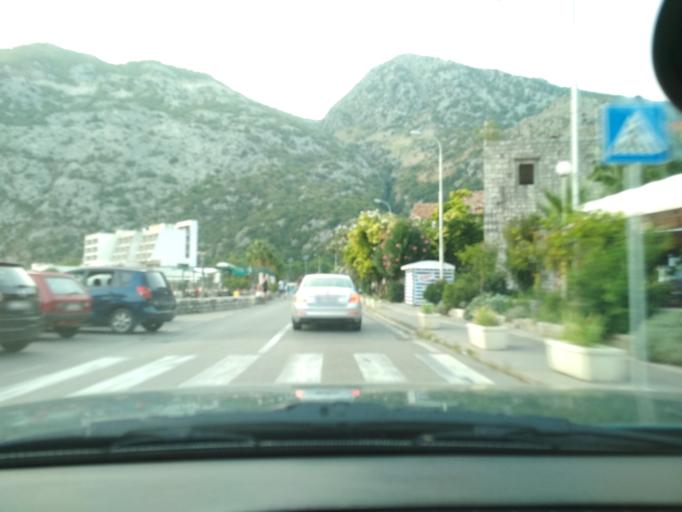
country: ME
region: Kotor
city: Risan
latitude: 42.5149
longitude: 18.6939
